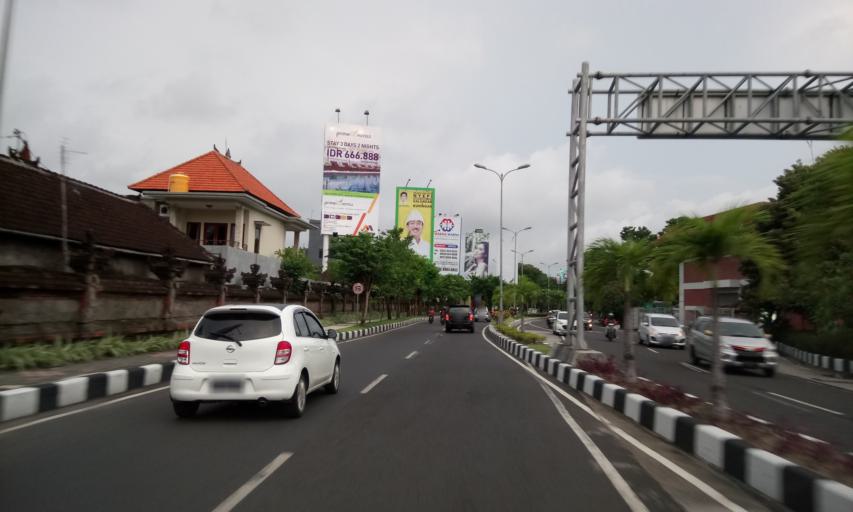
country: ID
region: Bali
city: Kelanabian
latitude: -8.7439
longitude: 115.1681
